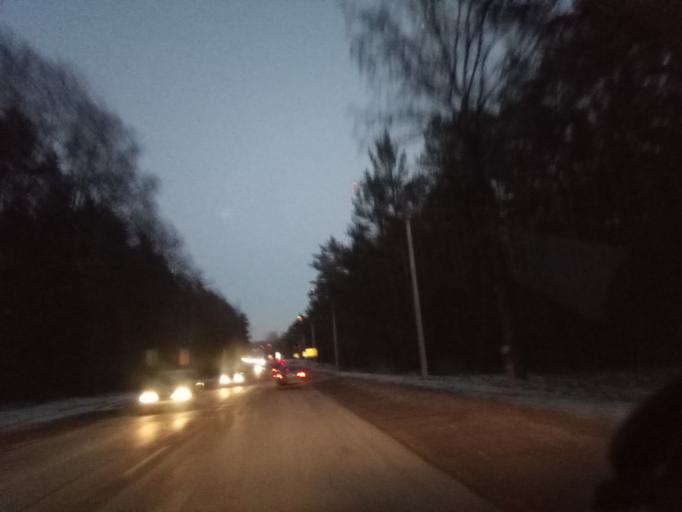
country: LT
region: Vilnius County
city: Lazdynai
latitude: 54.6372
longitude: 25.1755
